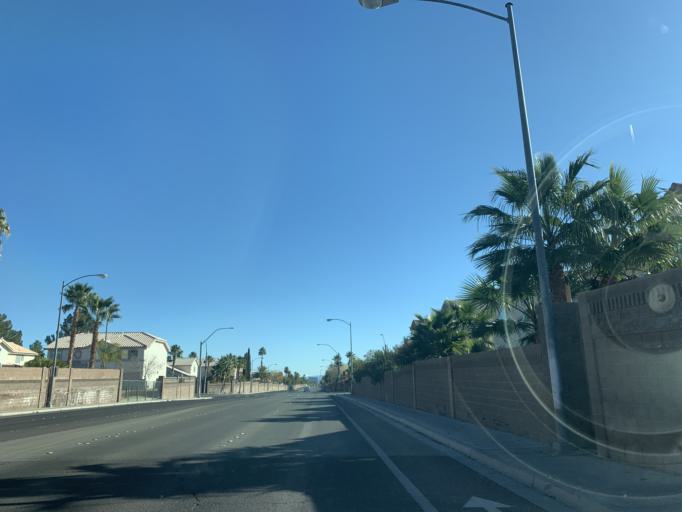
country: US
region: Nevada
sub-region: Clark County
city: Summerlin South
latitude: 36.1261
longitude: -115.3074
